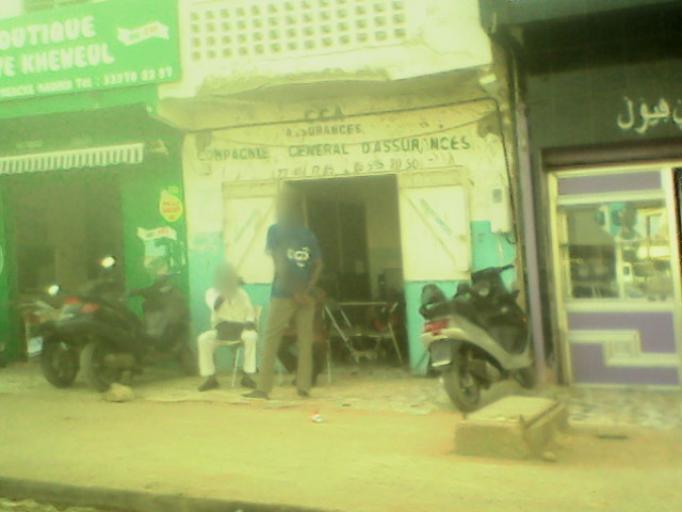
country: SN
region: Diourbel
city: Touba
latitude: 14.8573
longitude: -15.8788
